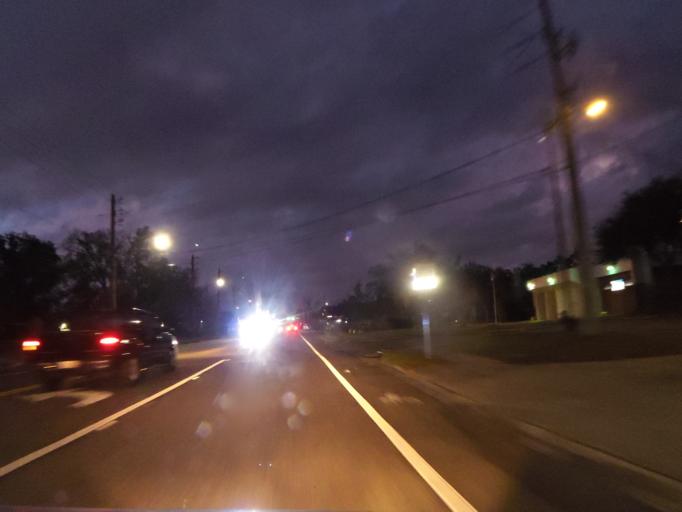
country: US
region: Florida
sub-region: Clay County
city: Bellair-Meadowbrook Terrace
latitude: 30.2463
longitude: -81.7385
